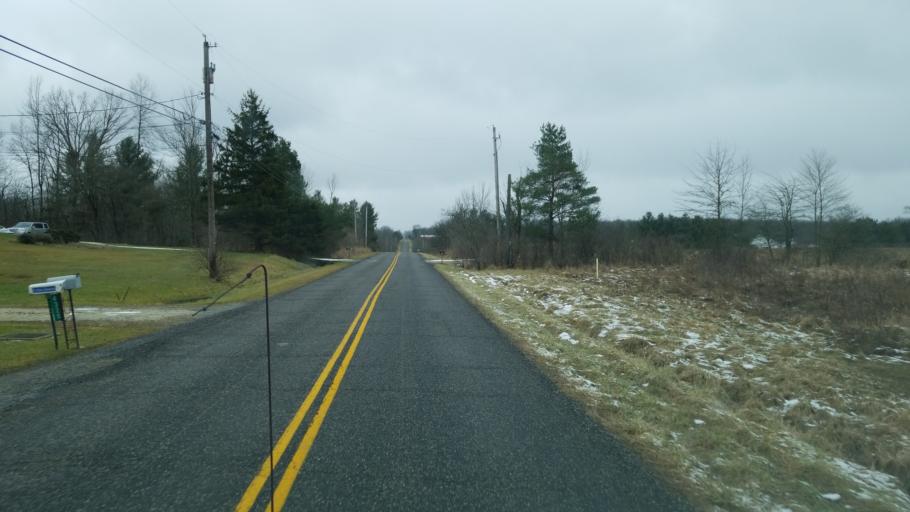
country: US
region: Ohio
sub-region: Portage County
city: Windham
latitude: 41.3365
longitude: -80.9835
